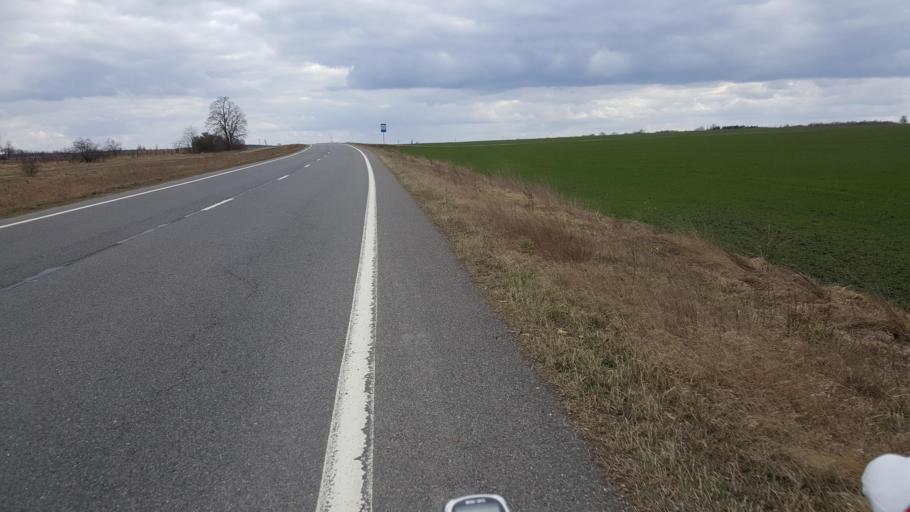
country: BY
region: Brest
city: Kamyanyets
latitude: 52.4388
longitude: 23.8297
